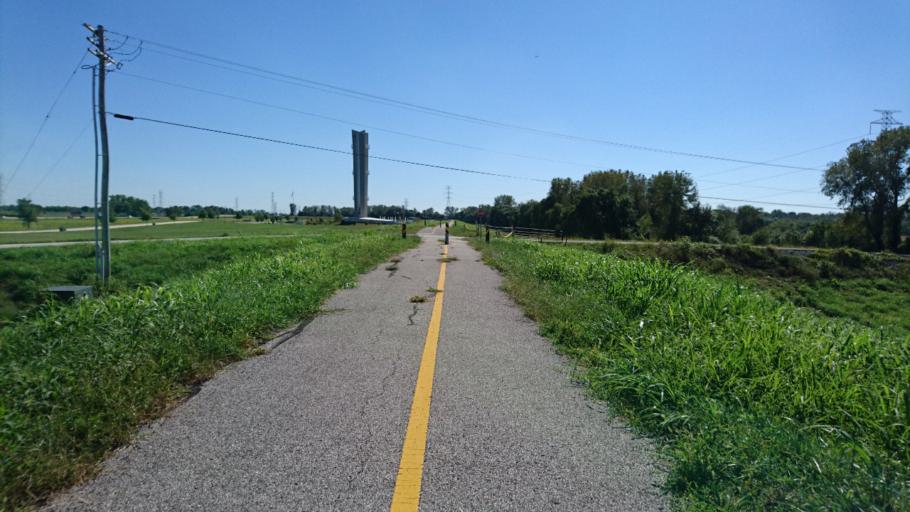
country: US
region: Illinois
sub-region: Madison County
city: Hartford
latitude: 38.8141
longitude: -90.1003
